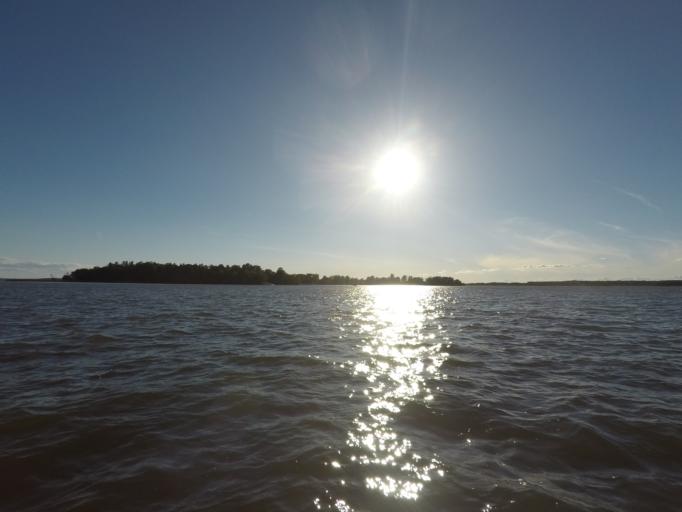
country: SE
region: Vaestmanland
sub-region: Vasteras
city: Vasteras
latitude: 59.5172
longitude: 16.5778
